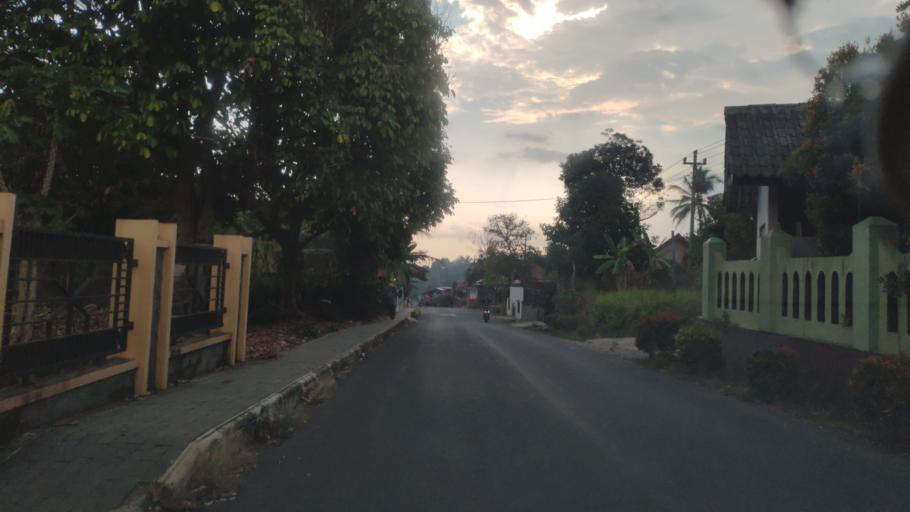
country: ID
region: Central Java
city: Purbalingga
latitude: -7.3535
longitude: 109.5445
